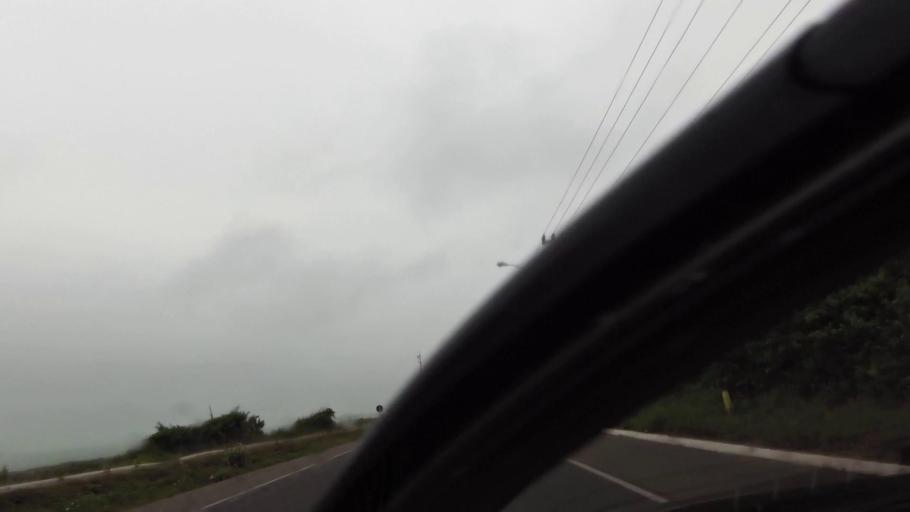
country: BR
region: Espirito Santo
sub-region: Guarapari
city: Guarapari
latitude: -20.7056
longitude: -40.5166
